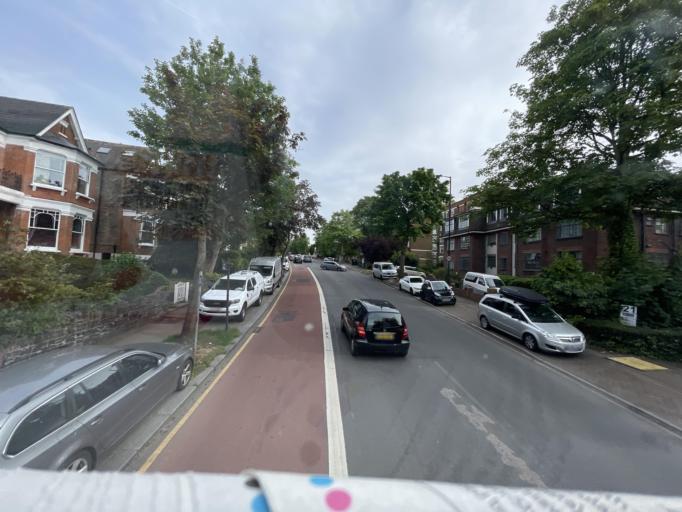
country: GB
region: England
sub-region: Greater London
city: Crouch End
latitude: 51.5968
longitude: -0.1454
